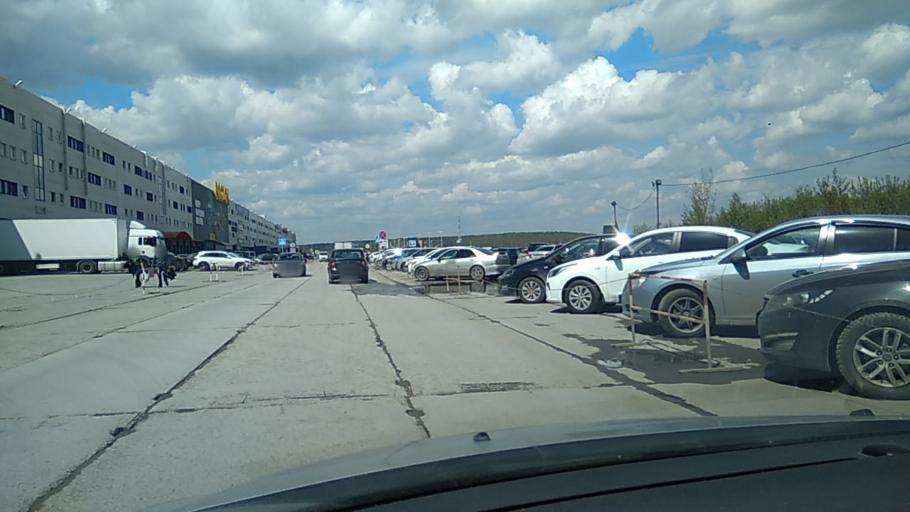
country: RU
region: Sverdlovsk
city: Istok
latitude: 56.7594
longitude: 60.7557
